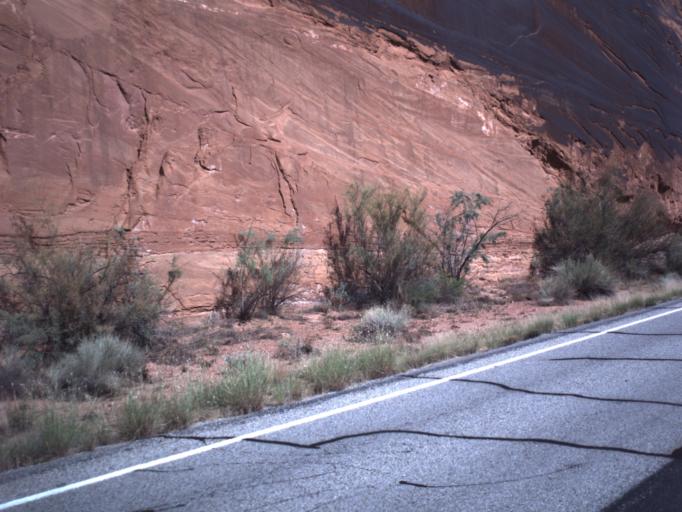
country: US
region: Utah
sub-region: Grand County
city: Moab
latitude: 38.5330
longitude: -109.6230
